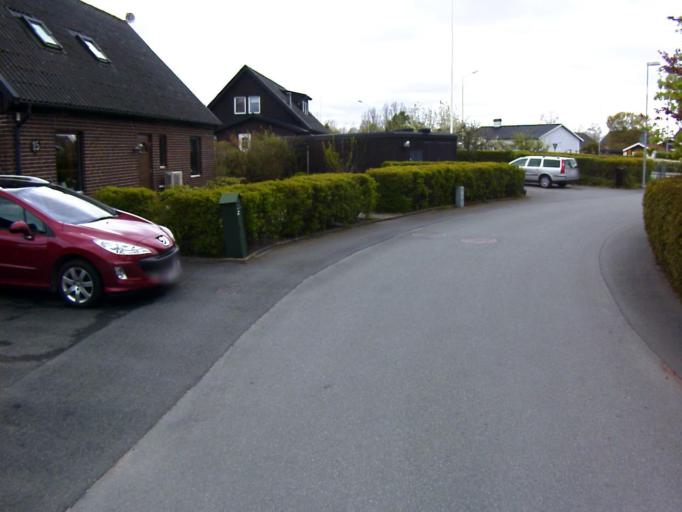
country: SE
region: Skane
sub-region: Kristianstads Kommun
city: Kristianstad
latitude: 56.0504
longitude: 14.1727
